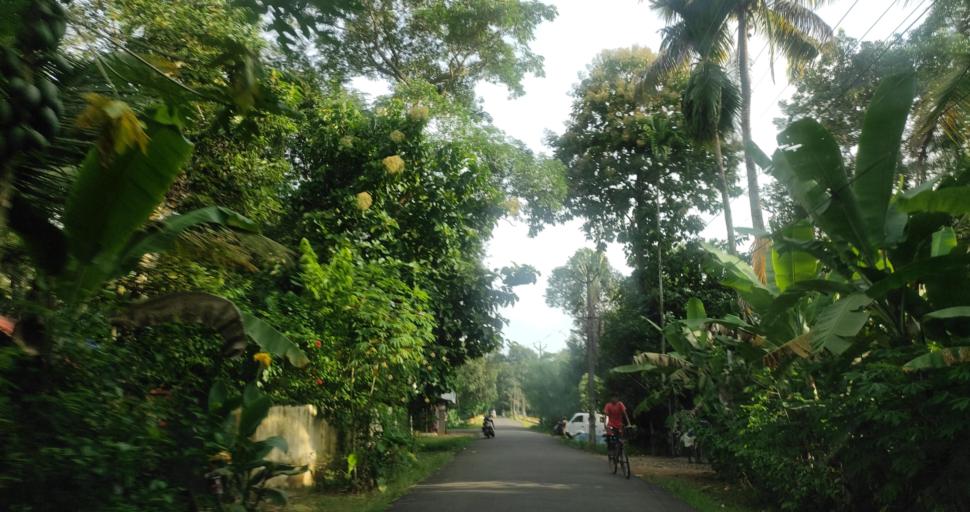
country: IN
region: Kerala
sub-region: Alappuzha
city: Shertallai
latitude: 9.6128
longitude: 76.3403
